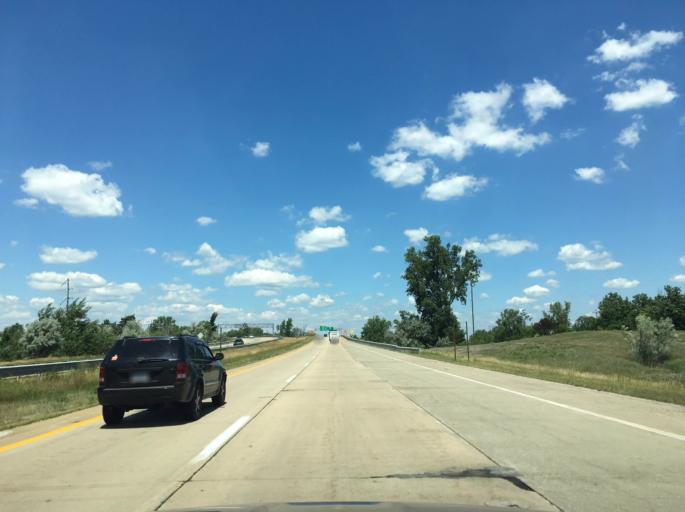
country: US
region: Michigan
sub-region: Midland County
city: Midland
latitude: 43.6052
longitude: -84.1611
